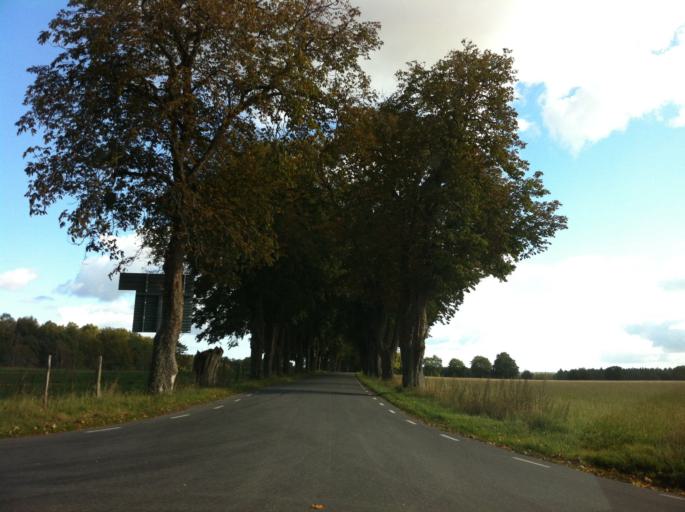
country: SE
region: Skane
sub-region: Kristianstads Kommun
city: Degeberga
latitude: 55.7146
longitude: 13.9674
